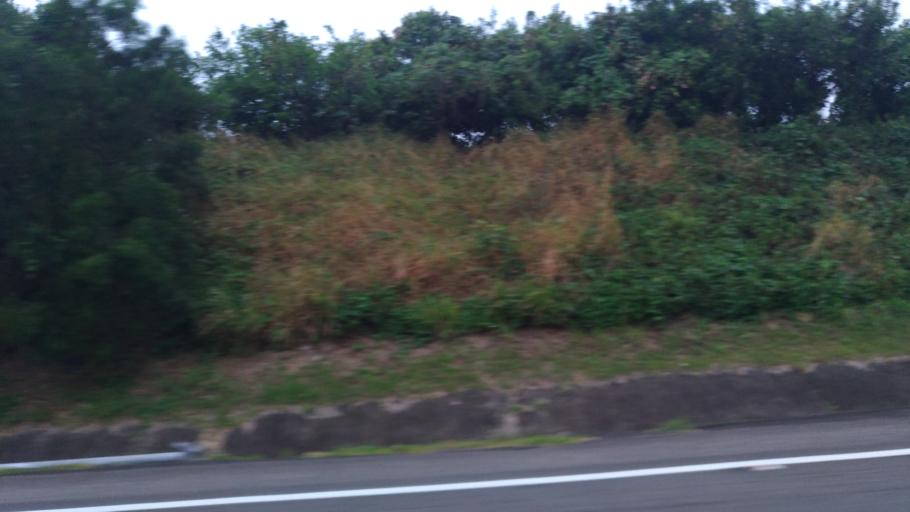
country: TW
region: Taiwan
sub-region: Hsinchu
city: Hsinchu
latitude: 24.7560
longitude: 120.9580
